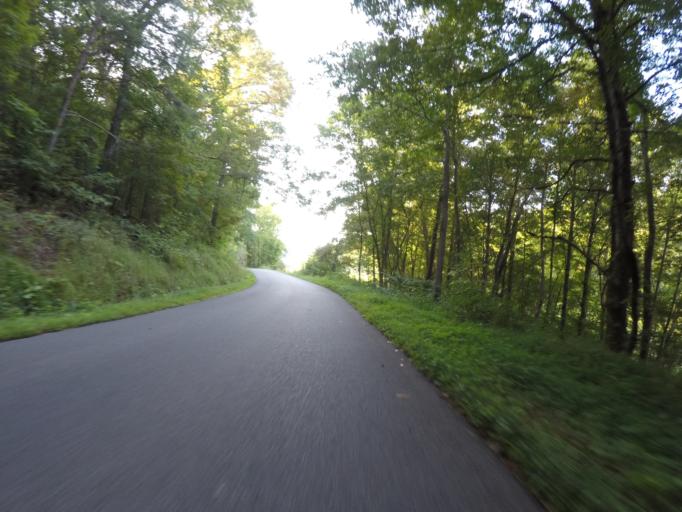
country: US
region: Ohio
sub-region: Lawrence County
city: Coal Grove
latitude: 38.5507
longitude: -82.5550
